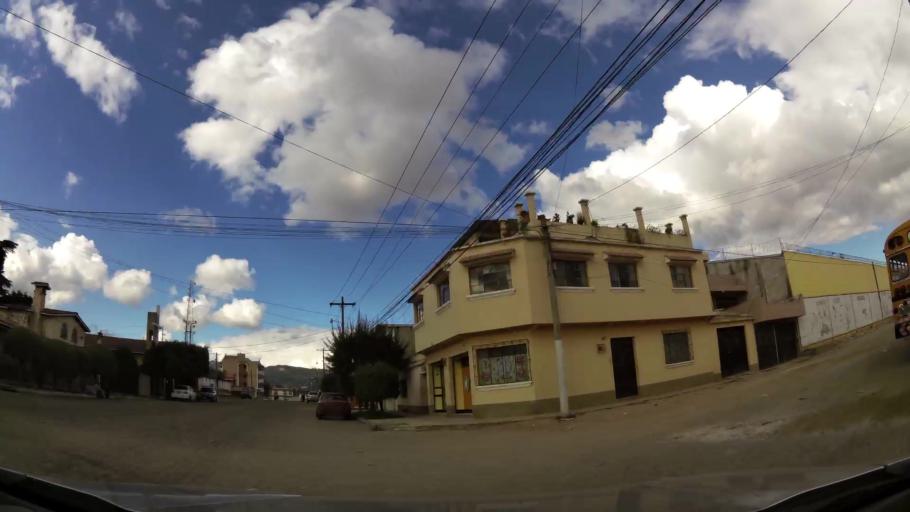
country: GT
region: Quetzaltenango
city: Quetzaltenango
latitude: 14.8495
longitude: -91.5254
